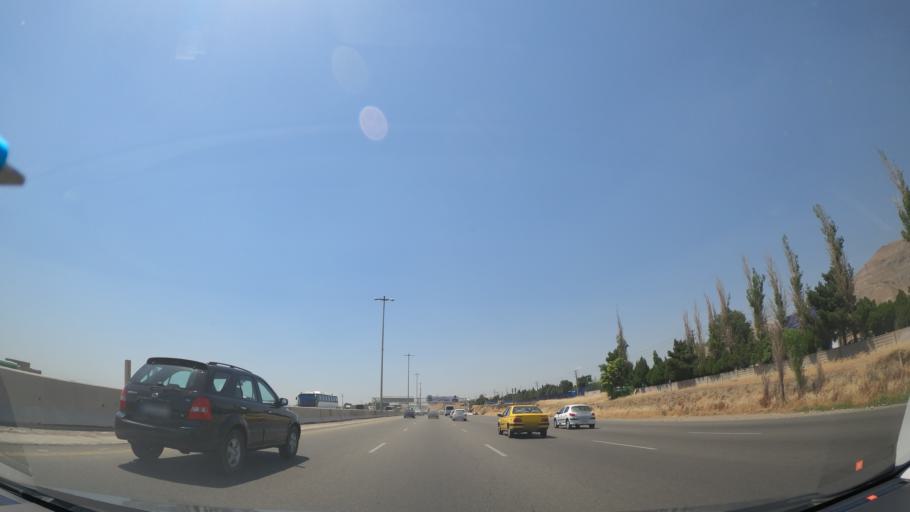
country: IR
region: Tehran
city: Shahr-e Qods
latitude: 35.7625
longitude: 51.0611
